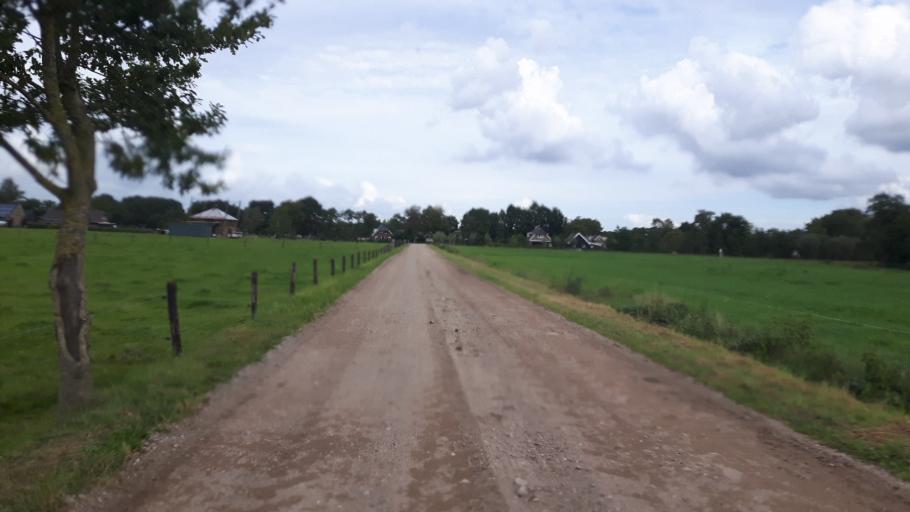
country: NL
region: Gelderland
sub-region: Gemeente Putten
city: Putten
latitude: 52.2597
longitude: 5.5591
